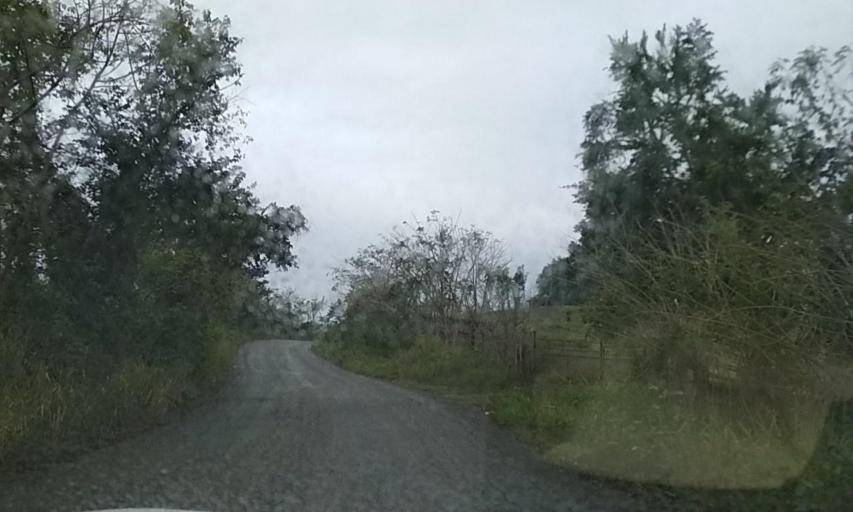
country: MX
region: Veracruz
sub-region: Coatzintla
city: Manuel Maria Contreras
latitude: 20.4531
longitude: -97.4745
